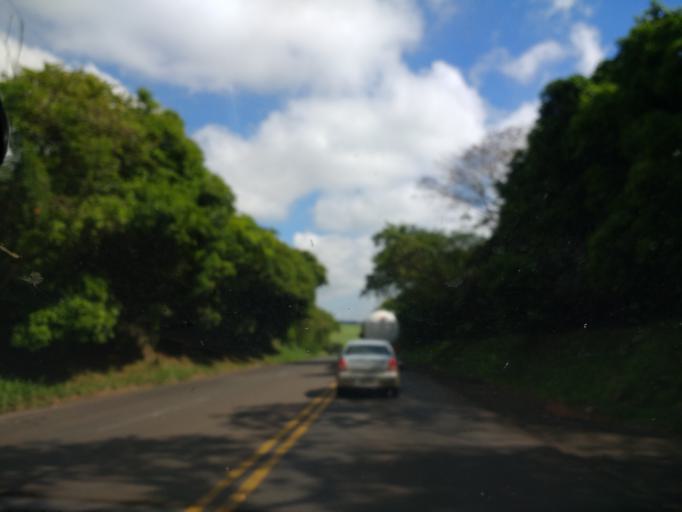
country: BR
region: Parana
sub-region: Cruzeiro Do Oeste
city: Cruzeiro do Oeste
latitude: -23.7635
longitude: -52.9986
